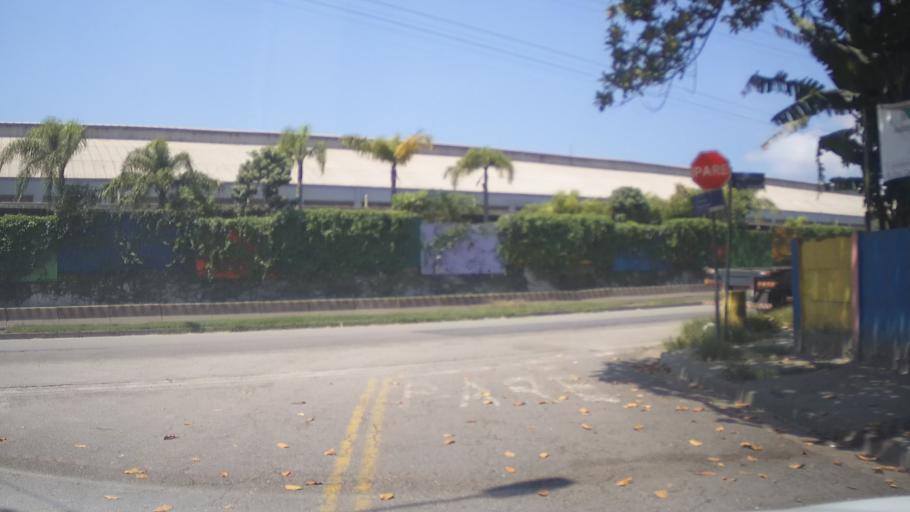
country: BR
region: Sao Paulo
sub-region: Guaruja
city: Guaruja
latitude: -23.9822
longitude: -46.2945
